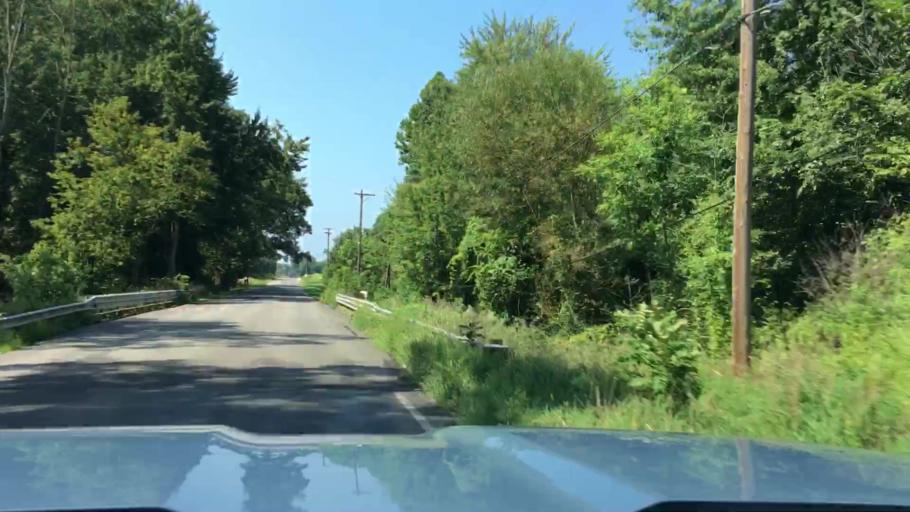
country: US
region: Michigan
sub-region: Saint Joseph County
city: Three Rivers
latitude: 41.9985
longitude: -85.5848
